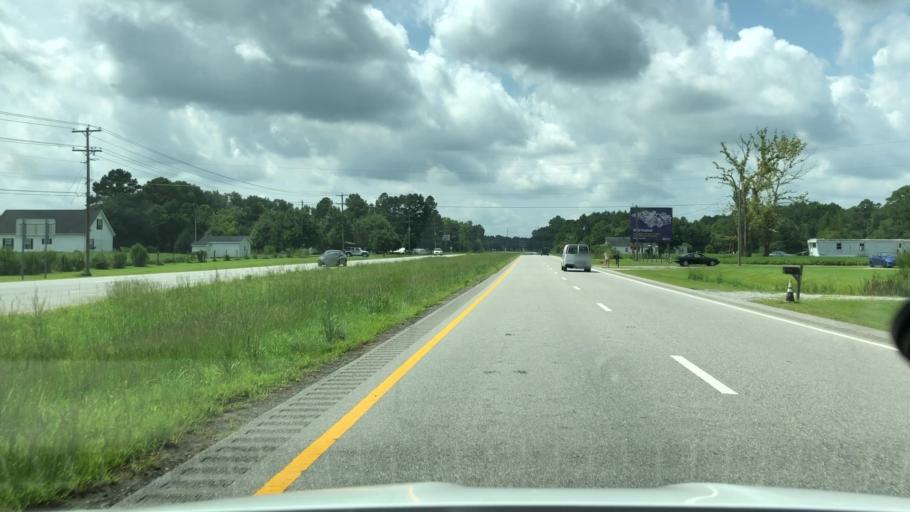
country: US
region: North Carolina
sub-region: Beaufort County
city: Washington
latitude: 35.4827
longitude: -77.1126
